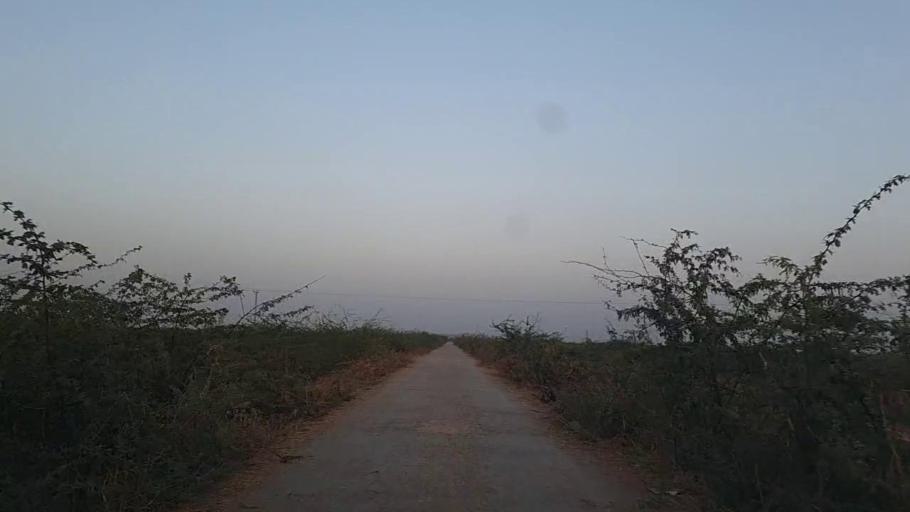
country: PK
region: Sindh
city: Naukot
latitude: 24.7200
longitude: 69.2945
